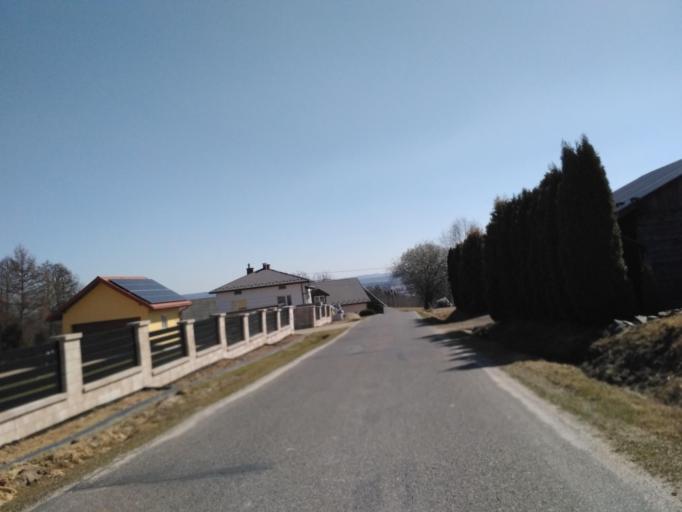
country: PL
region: Subcarpathian Voivodeship
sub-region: Powiat brzozowski
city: Orzechowka
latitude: 49.7332
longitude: 21.9251
